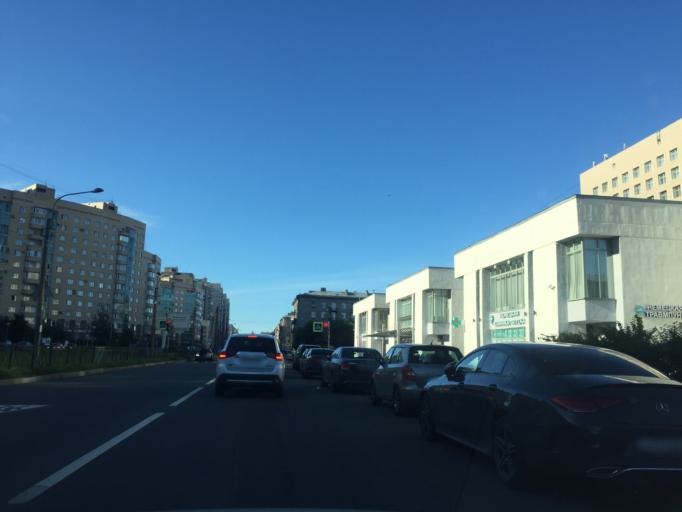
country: RU
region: St.-Petersburg
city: Kupchino
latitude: 59.8683
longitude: 30.3139
